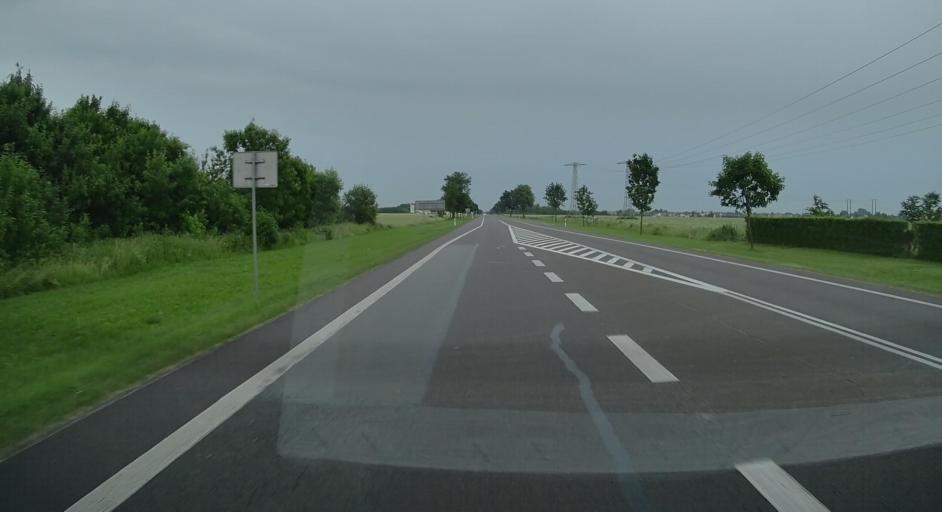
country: PL
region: Lublin Voivodeship
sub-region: Powiat bialski
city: Miedzyrzec Podlaski
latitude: 52.0001
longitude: 22.7851
